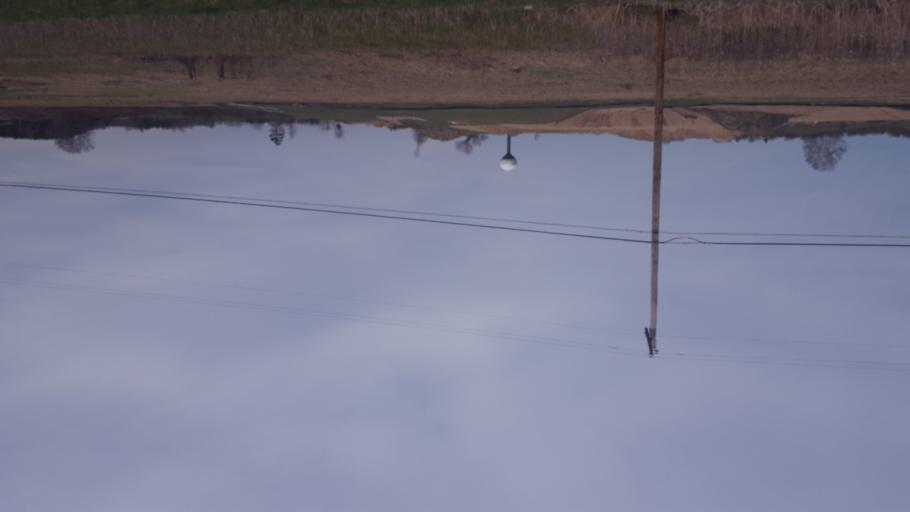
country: US
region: Michigan
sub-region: Clare County
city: Clare
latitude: 43.8482
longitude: -84.7682
